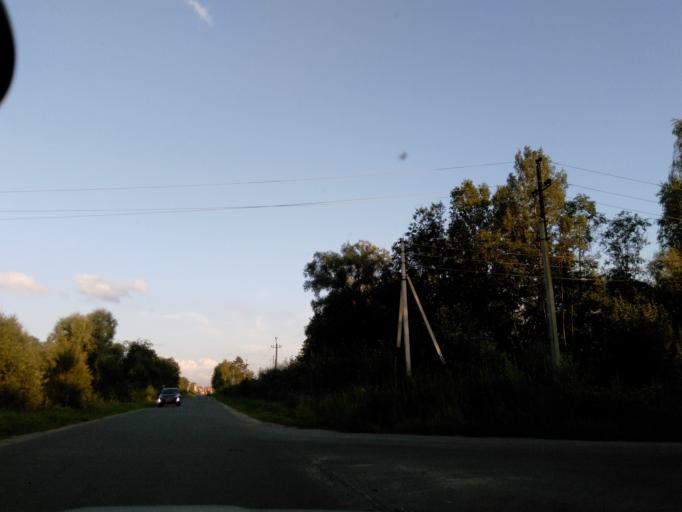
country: RU
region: Tverskaya
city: Konakovo
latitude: 56.6832
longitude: 36.7021
